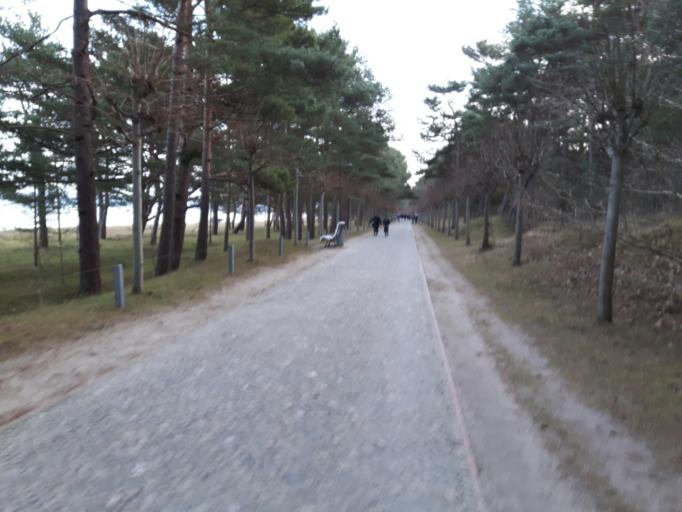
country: DE
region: Mecklenburg-Vorpommern
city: Ostseebad Binz
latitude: 54.4166
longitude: 13.5946
